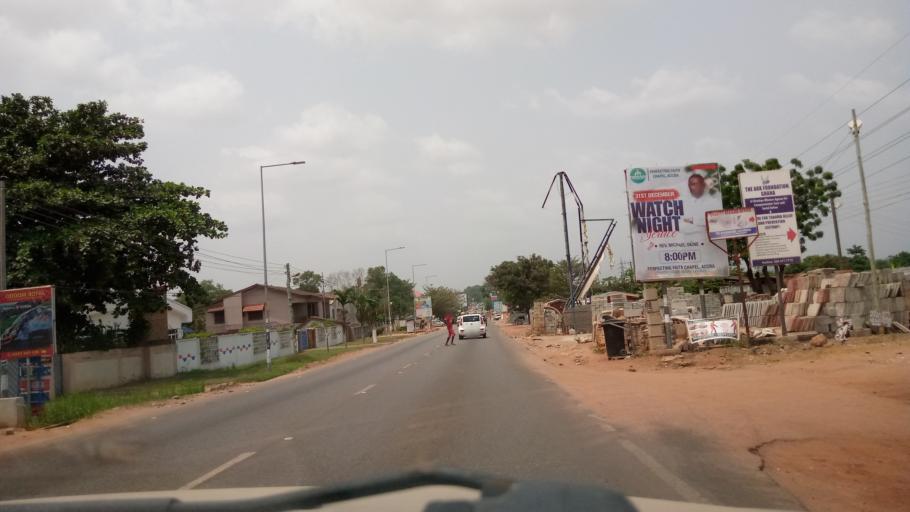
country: GH
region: Greater Accra
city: Dome
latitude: 5.6675
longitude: -0.2109
